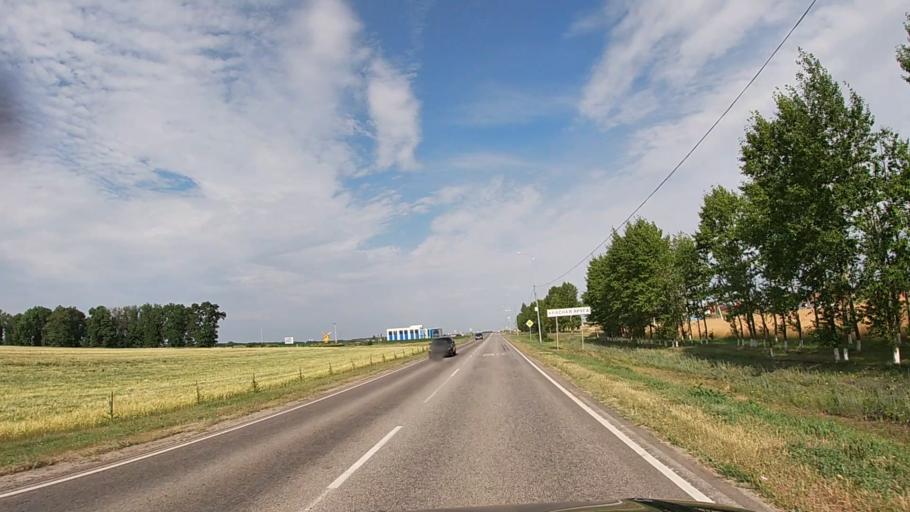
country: RU
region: Belgorod
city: Krasnaya Yaruga
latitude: 50.7959
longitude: 35.6982
